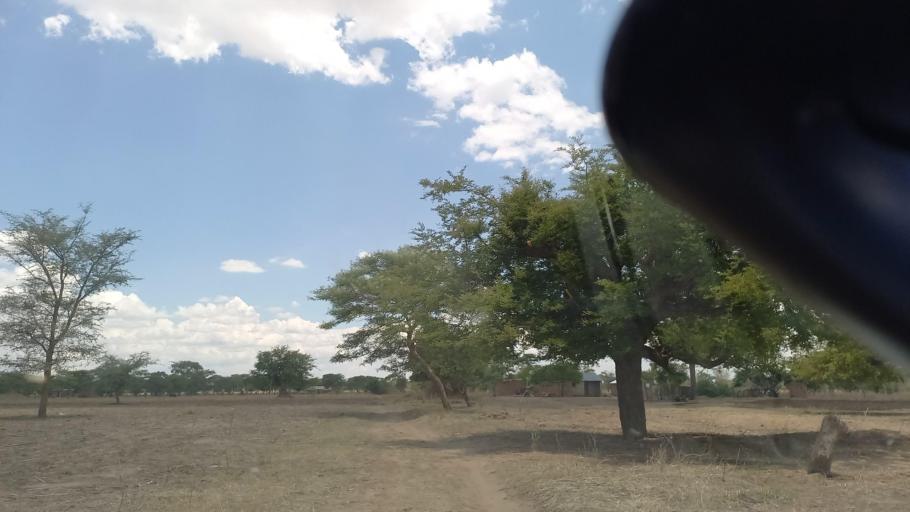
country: ZM
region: Southern
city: Mazabuka
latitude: -16.1216
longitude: 27.7768
